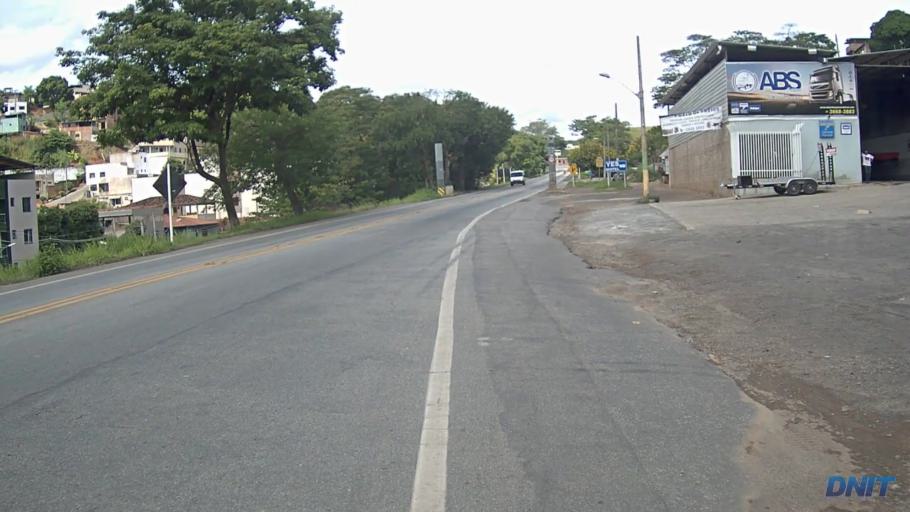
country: BR
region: Minas Gerais
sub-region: Ipatinga
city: Ipatinga
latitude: -19.4619
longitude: -42.5309
